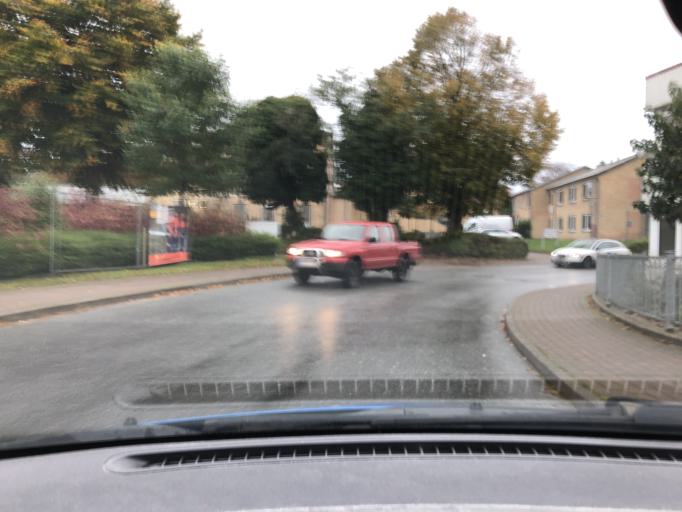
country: DE
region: Schleswig-Holstein
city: Fahrdorf
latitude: 54.5004
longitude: 9.5999
